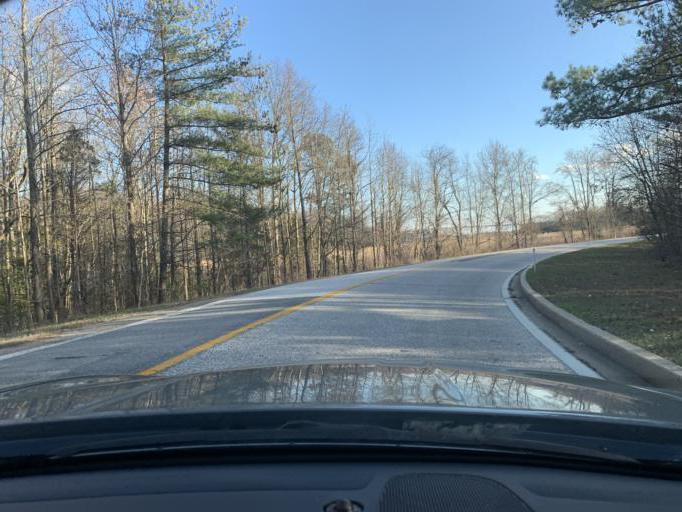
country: US
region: Maryland
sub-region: Anne Arundel County
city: Cape Saint Claire
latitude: 39.0181
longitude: -76.4078
